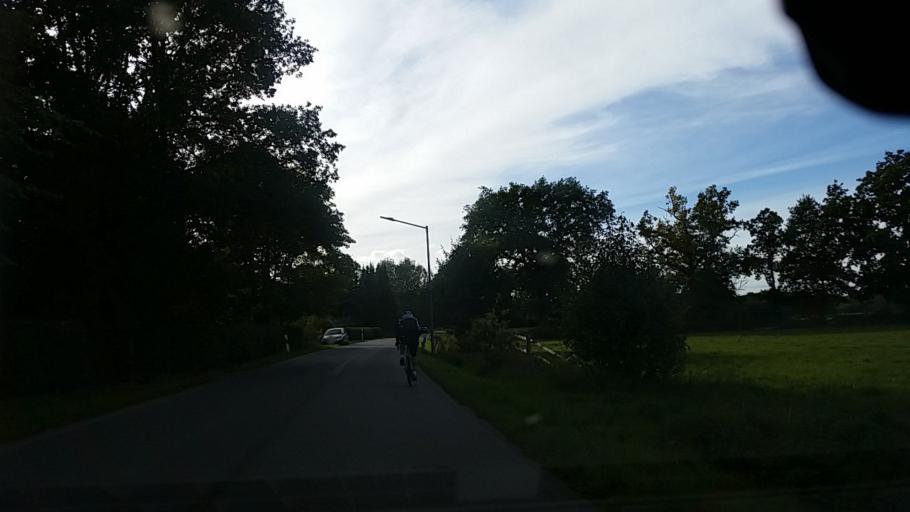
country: DE
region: Schleswig-Holstein
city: Jersbek
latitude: 53.7359
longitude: 10.1872
